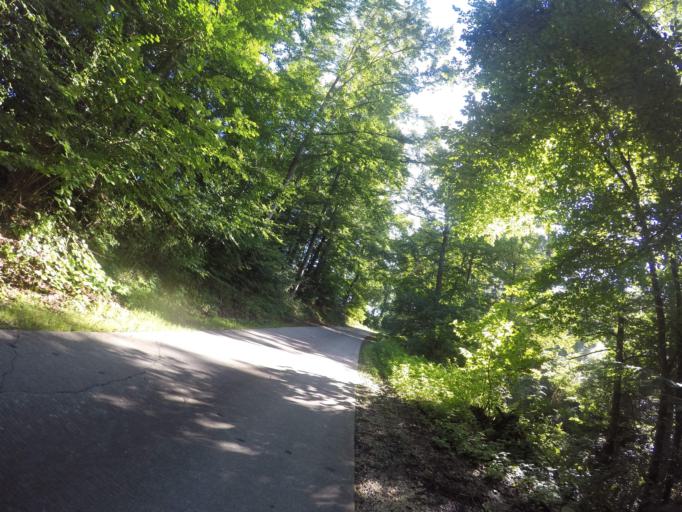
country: DE
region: Baden-Wuerttemberg
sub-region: Tuebingen Region
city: Schelklingen
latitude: 48.3923
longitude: 9.7367
